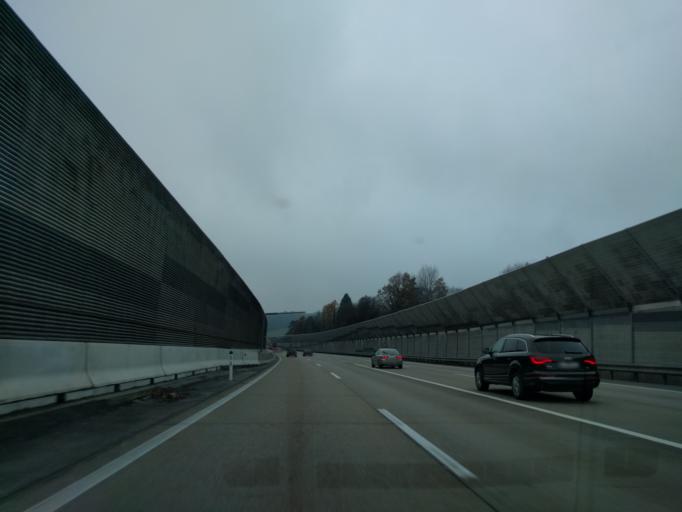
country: AT
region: Lower Austria
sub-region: Politischer Bezirk Sankt Polten
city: Eichgraben
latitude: 48.1581
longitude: 15.9569
